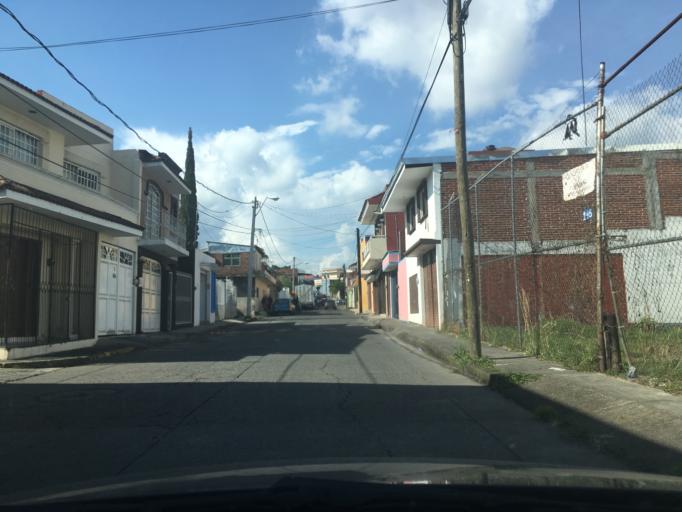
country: MX
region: Michoacan
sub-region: Uruapan
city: Uruapan
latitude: 19.4087
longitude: -102.0640
